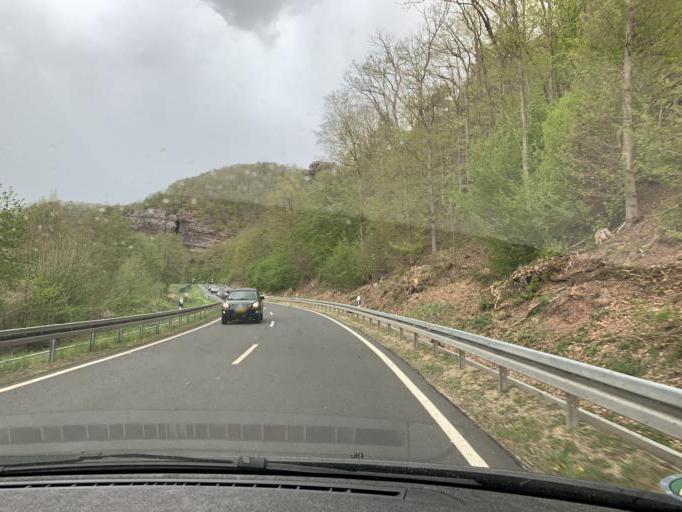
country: DE
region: North Rhine-Westphalia
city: Heimbach
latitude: 50.6575
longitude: 6.4965
